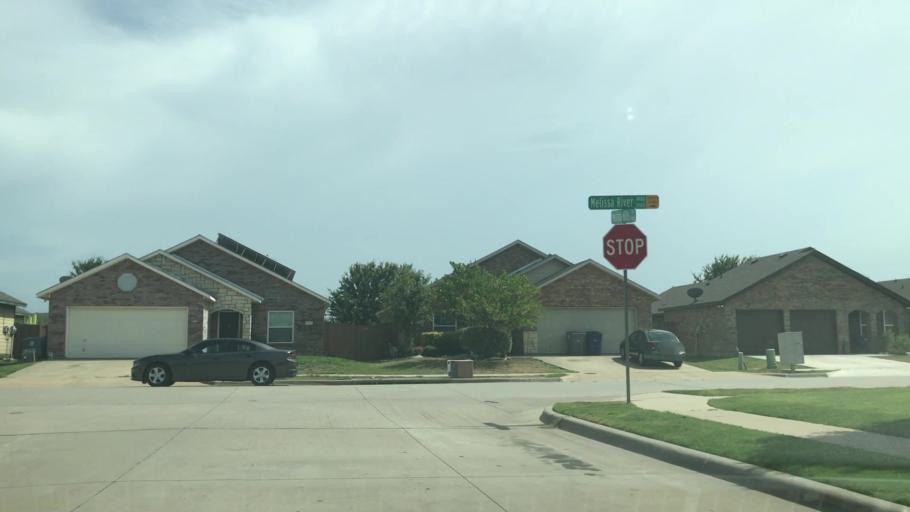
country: US
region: Texas
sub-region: Dallas County
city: Cockrell Hill
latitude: 32.7841
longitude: -96.8717
